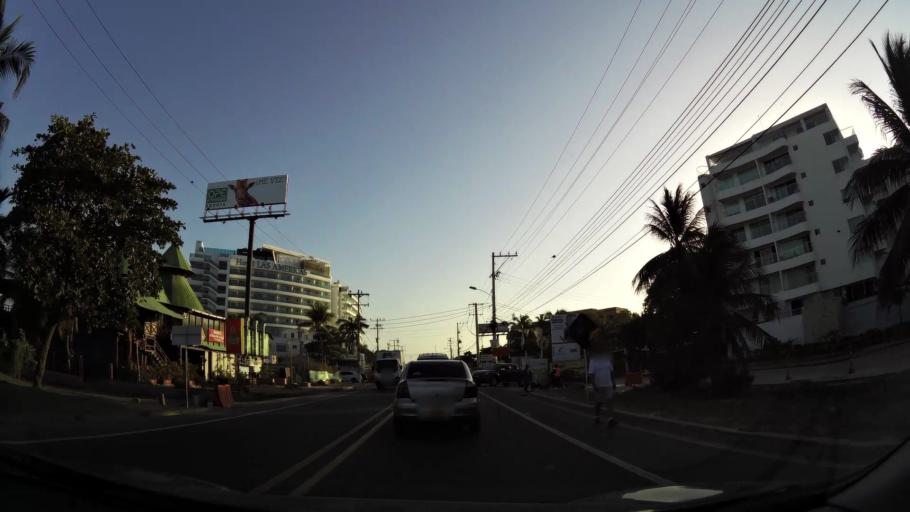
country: CO
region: Bolivar
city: Cartagena
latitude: 10.4579
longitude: -75.5085
